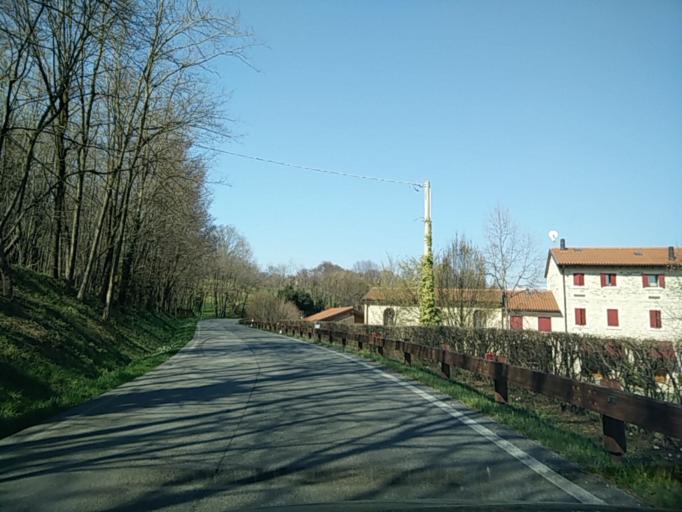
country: IT
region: Veneto
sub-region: Provincia di Treviso
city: Nervesa della Battaglia
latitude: 45.8315
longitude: 12.2014
